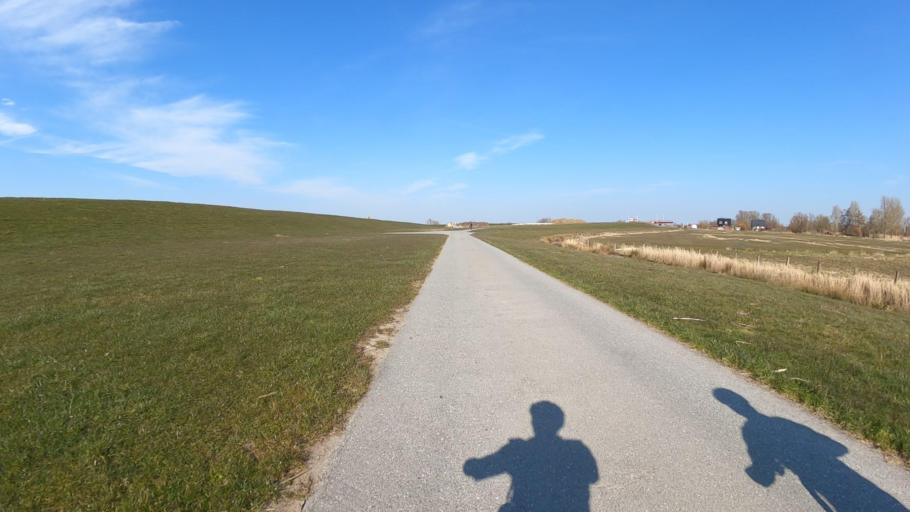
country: DE
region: Schleswig-Holstein
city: Seestermuhe
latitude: 53.6673
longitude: 9.5556
